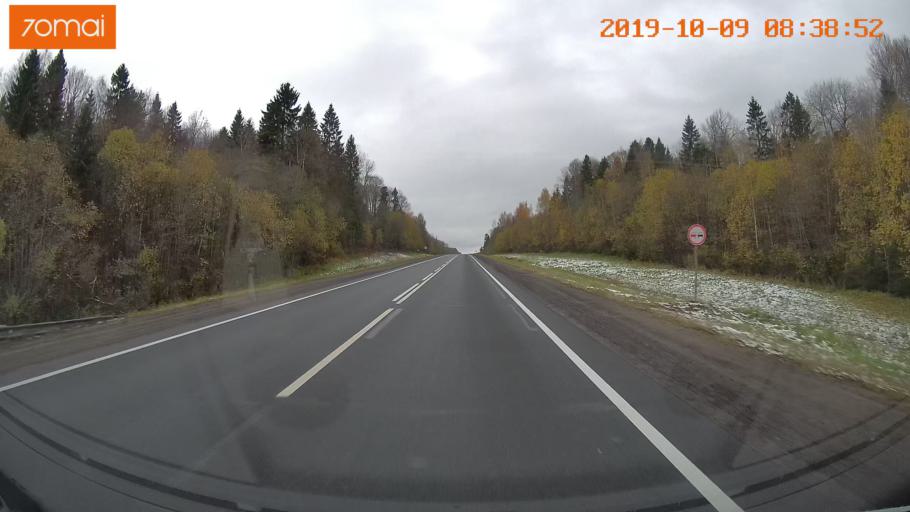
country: RU
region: Vologda
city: Gryazovets
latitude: 58.9630
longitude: 40.1602
